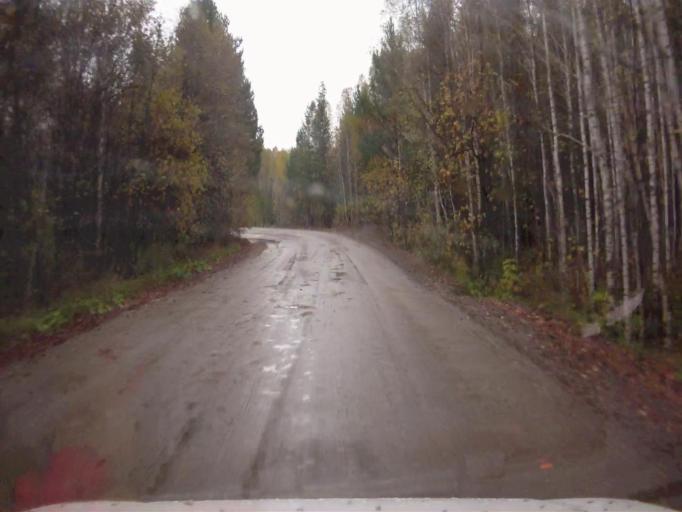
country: RU
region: Chelyabinsk
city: Kyshtym
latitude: 55.8236
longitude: 60.4833
